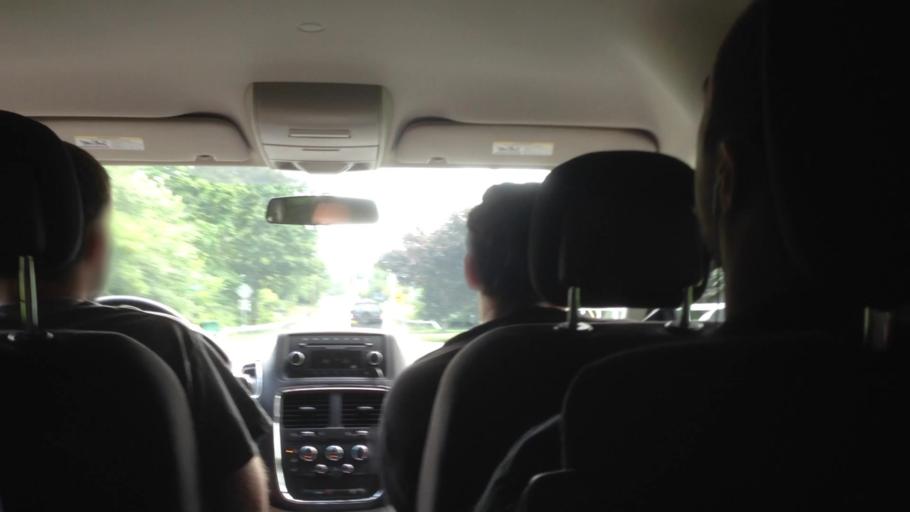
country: US
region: New York
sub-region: Dutchess County
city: Tivoli
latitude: 42.0596
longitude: -73.8989
